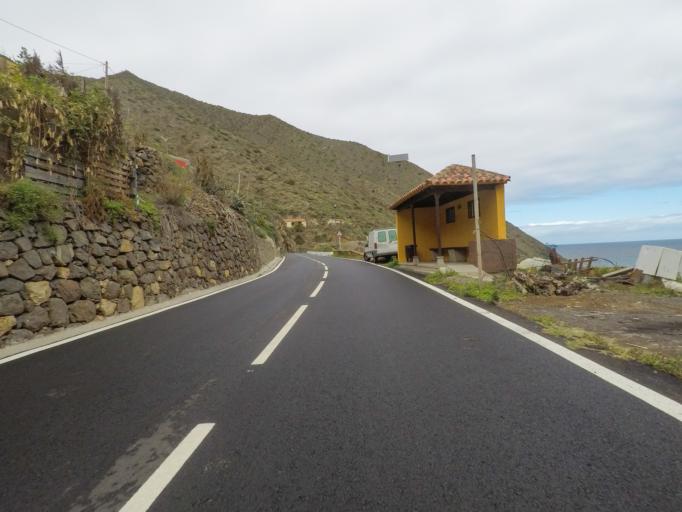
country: ES
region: Canary Islands
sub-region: Provincia de Santa Cruz de Tenerife
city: Vallehermosa
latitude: 28.1991
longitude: -17.2563
